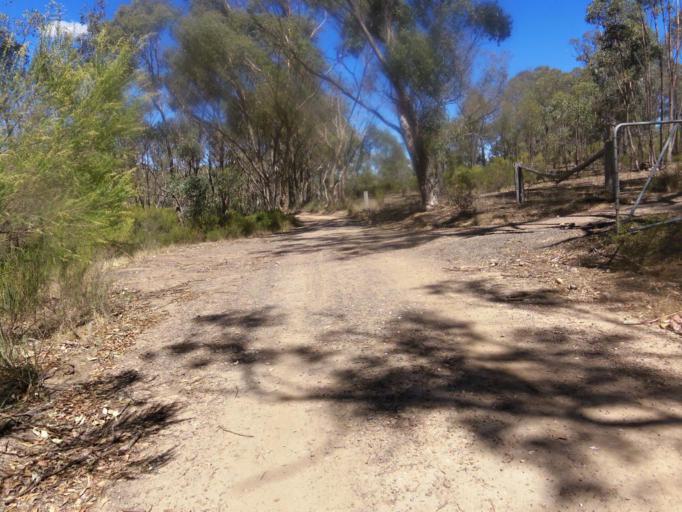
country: AU
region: Victoria
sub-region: Mount Alexander
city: Castlemaine
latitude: -37.0594
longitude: 144.1914
